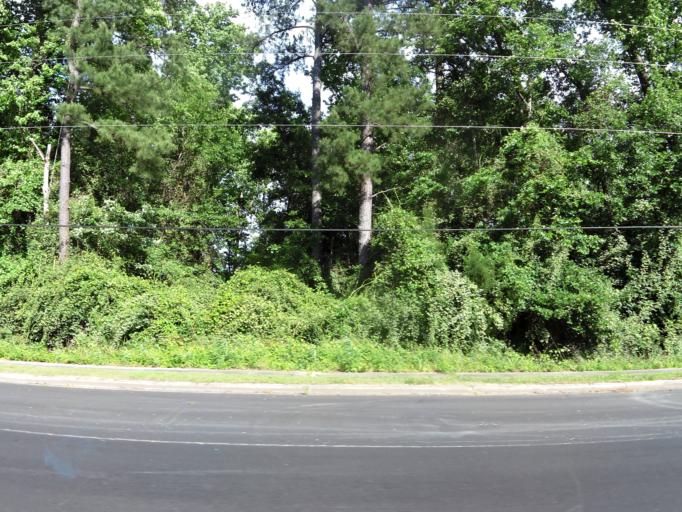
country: US
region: South Carolina
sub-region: Allendale County
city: Fairfax
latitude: 32.9728
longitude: -81.2318
